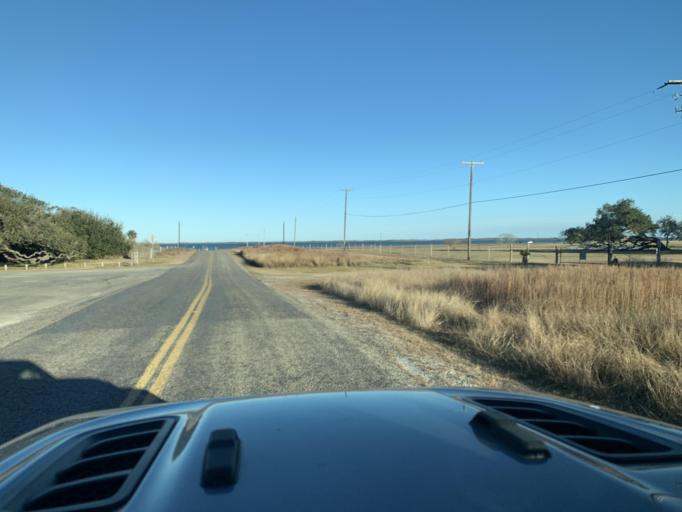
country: US
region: Texas
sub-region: Aransas County
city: Fulton
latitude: 28.1517
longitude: -96.9772
